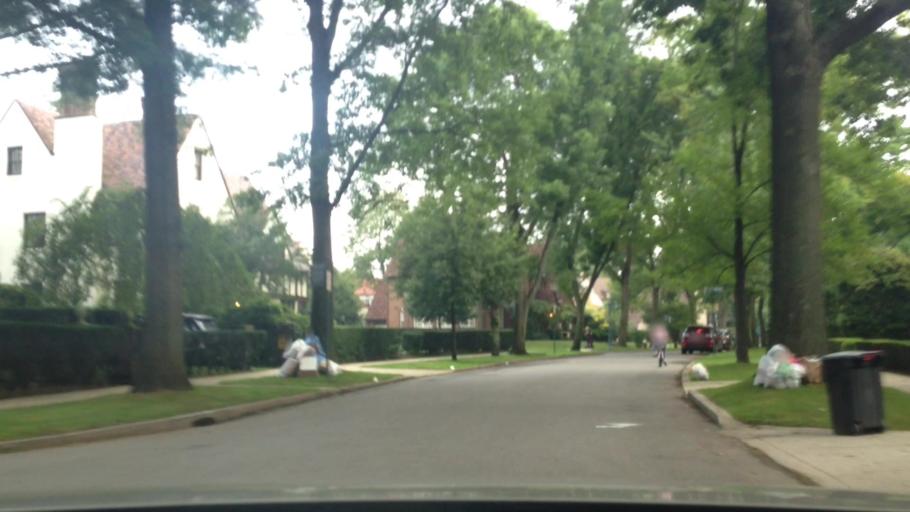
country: US
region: New York
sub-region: Queens County
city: Borough of Queens
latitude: 40.7151
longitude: -73.8448
